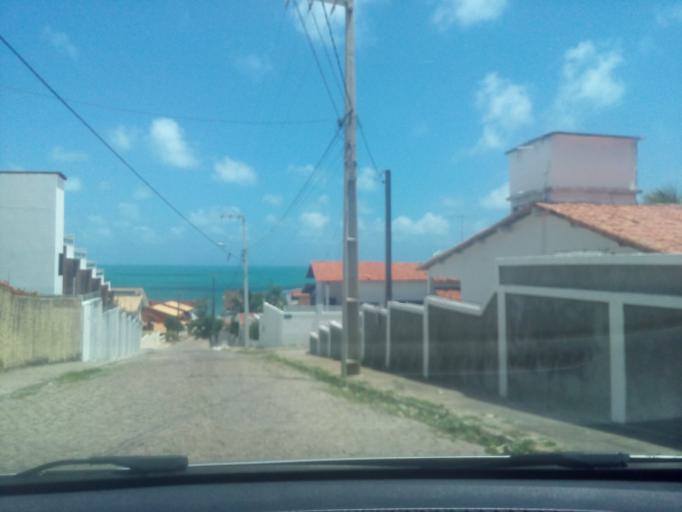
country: BR
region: Rio Grande do Norte
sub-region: Parnamirim
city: Parnamirim
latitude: -5.9688
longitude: -35.1310
